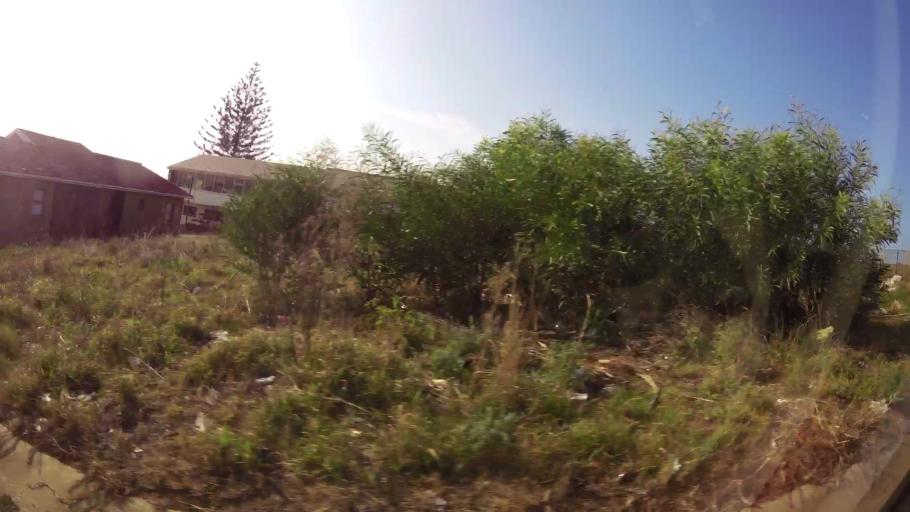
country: ZA
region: Eastern Cape
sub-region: Nelson Mandela Bay Metropolitan Municipality
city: Port Elizabeth
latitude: -33.9263
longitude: 25.5388
